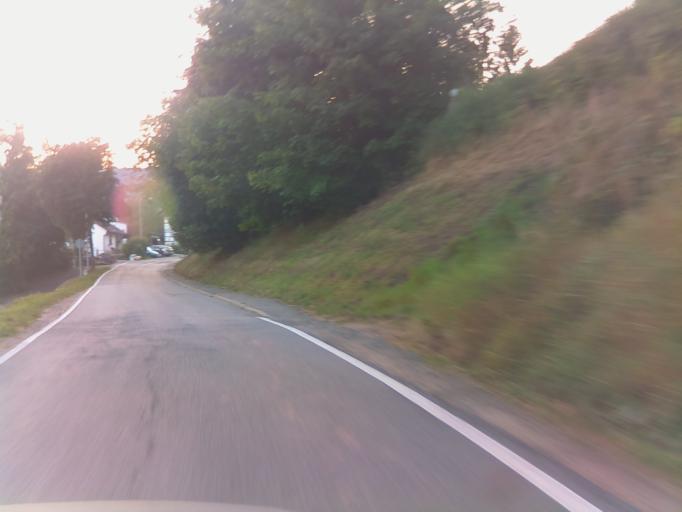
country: DE
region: Hesse
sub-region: Regierungsbezirk Darmstadt
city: Wald-Michelbach
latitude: 49.5996
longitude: 8.8392
